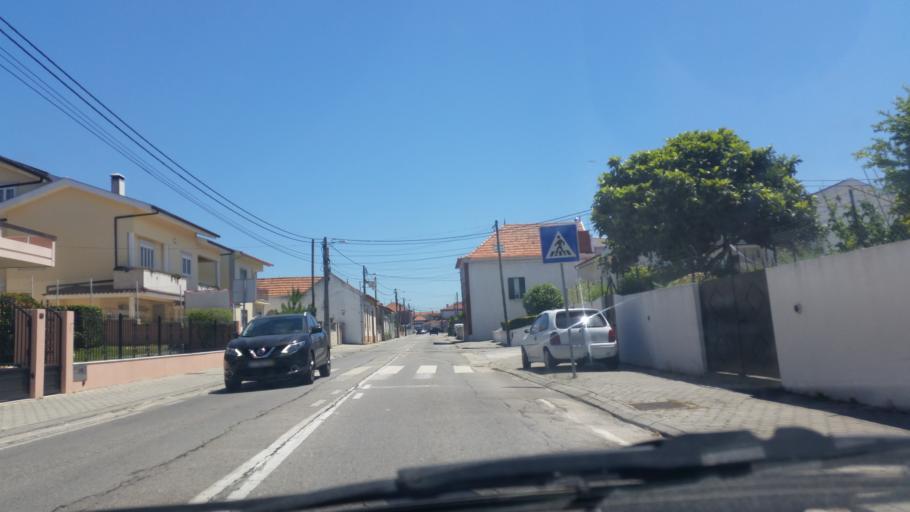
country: PT
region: Aveiro
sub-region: Aveiro
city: Aveiro
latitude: 40.6459
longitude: -8.6257
